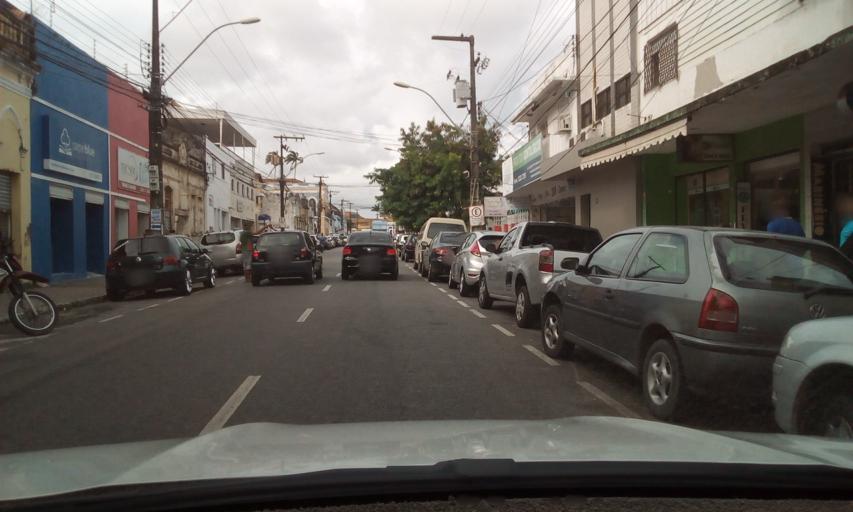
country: BR
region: Paraiba
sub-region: Joao Pessoa
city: Joao Pessoa
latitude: -7.1176
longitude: -34.8830
